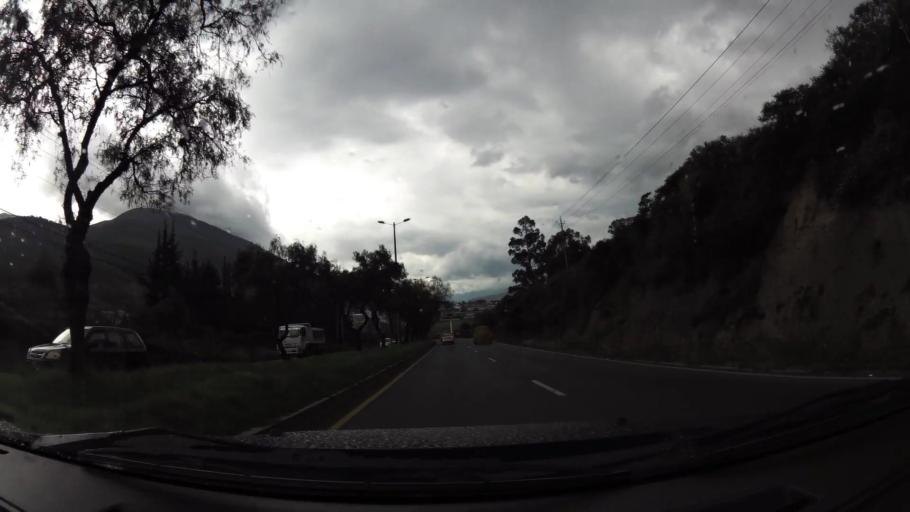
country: EC
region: Pichincha
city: Quito
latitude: -0.0810
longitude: -78.4821
